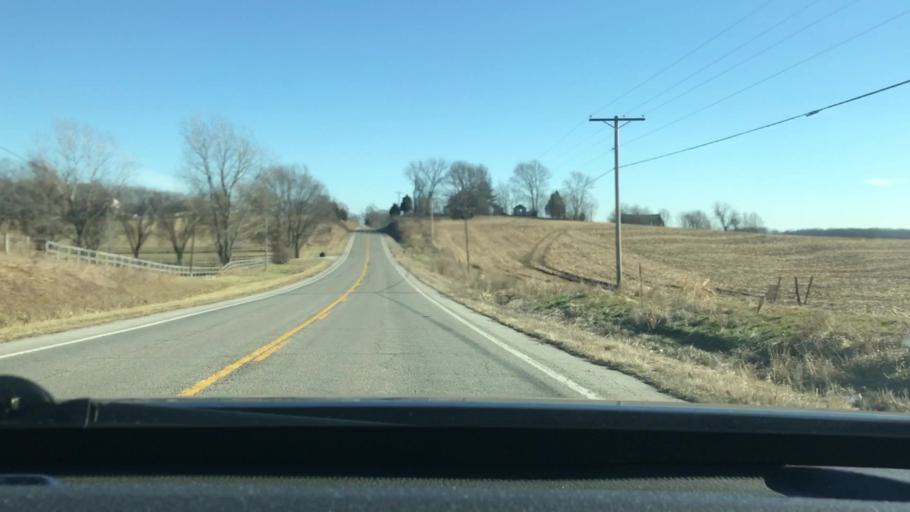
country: US
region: Missouri
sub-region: Platte County
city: Platte City
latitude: 39.3678
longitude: -94.8311
